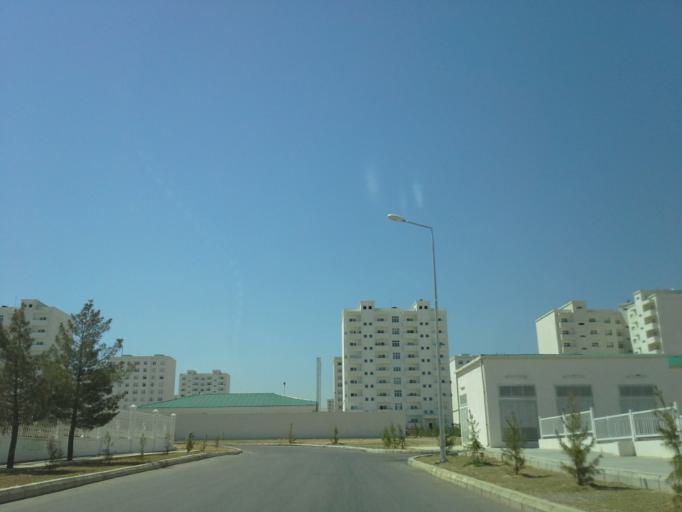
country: TM
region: Ahal
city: Ashgabat
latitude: 37.8925
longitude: 58.4074
